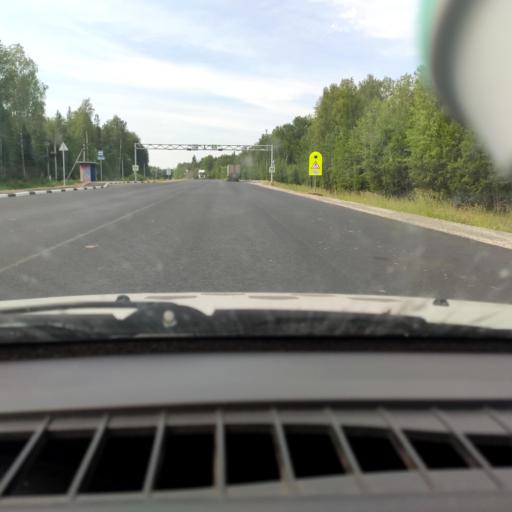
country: RU
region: Perm
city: Siva
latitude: 58.5489
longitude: 53.9093
